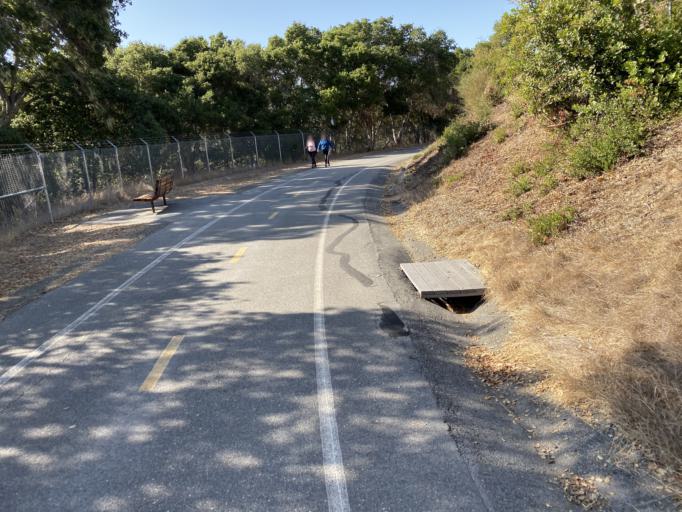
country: US
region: California
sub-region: San Mateo County
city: Highlands-Baywood Park
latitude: 37.5244
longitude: -122.3603
